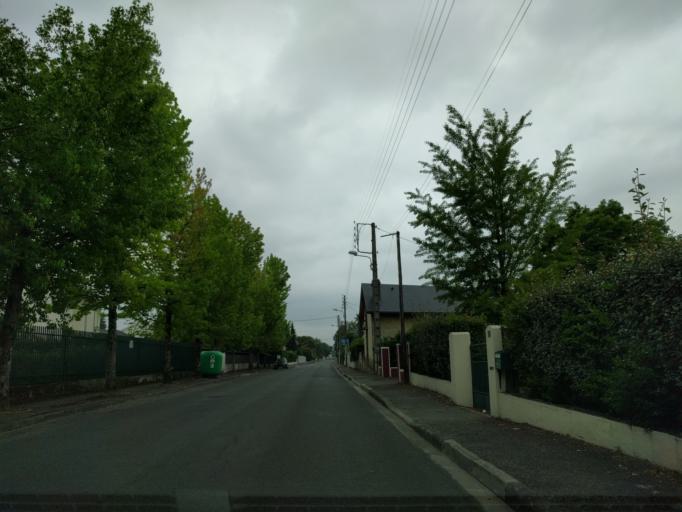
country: FR
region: Midi-Pyrenees
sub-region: Departement des Hautes-Pyrenees
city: Tarbes
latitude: 43.2275
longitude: 0.0644
